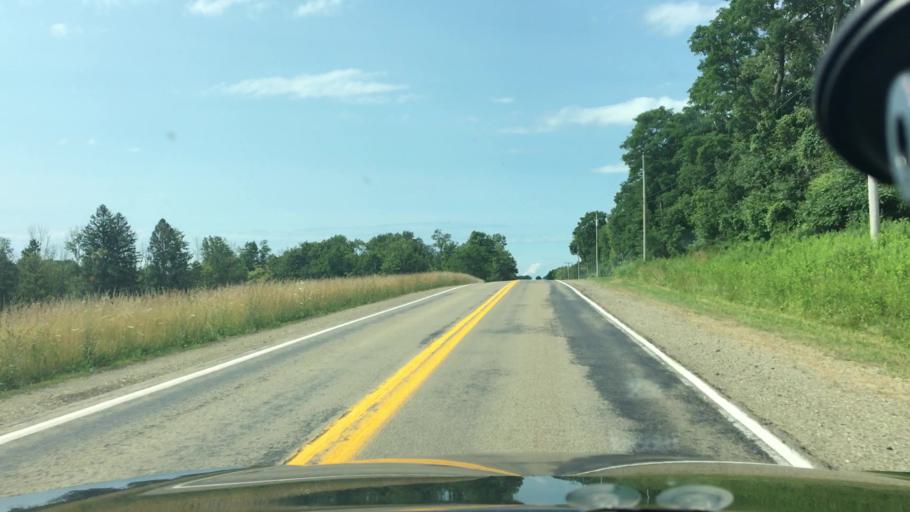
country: US
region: New York
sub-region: Chautauqua County
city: Lakewood
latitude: 42.1895
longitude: -79.3491
